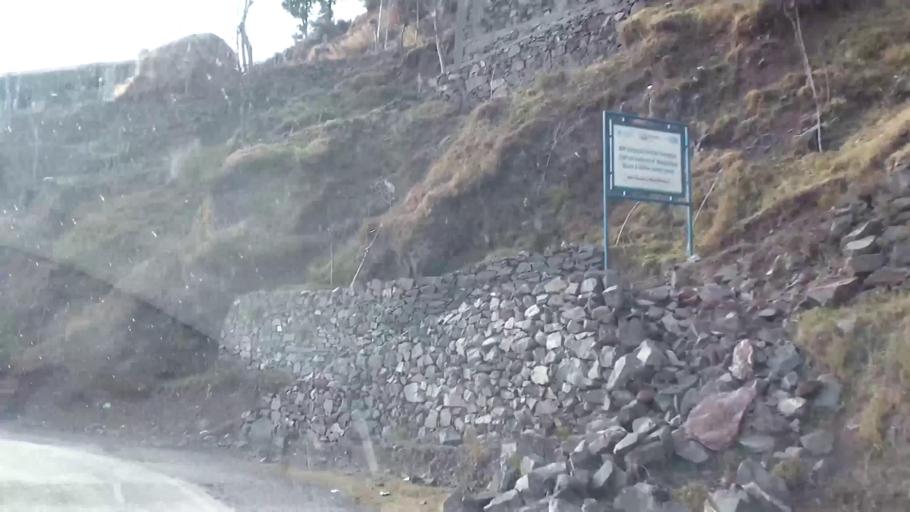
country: PK
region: Azad Kashmir
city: Muzaffarabad
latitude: 34.3690
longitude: 73.5156
